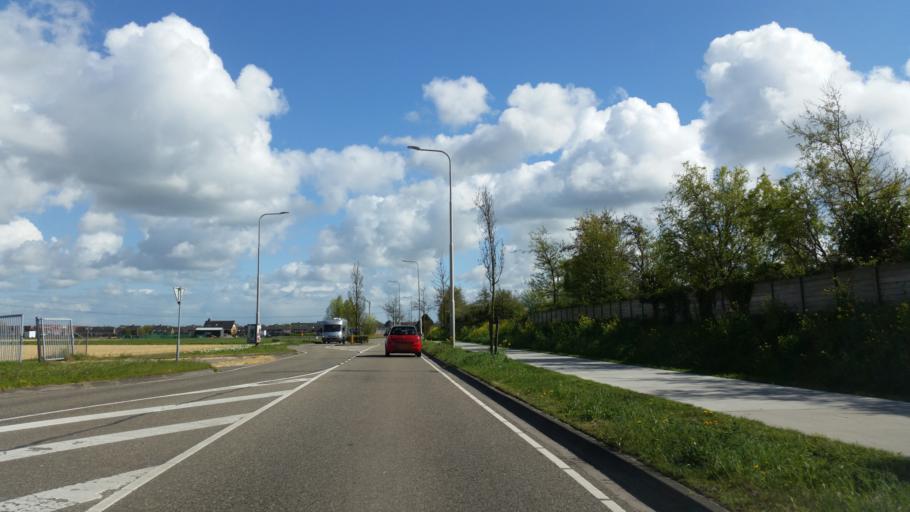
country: NL
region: South Holland
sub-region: Gemeente Teylingen
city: Voorhout
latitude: 52.2273
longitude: 4.5004
